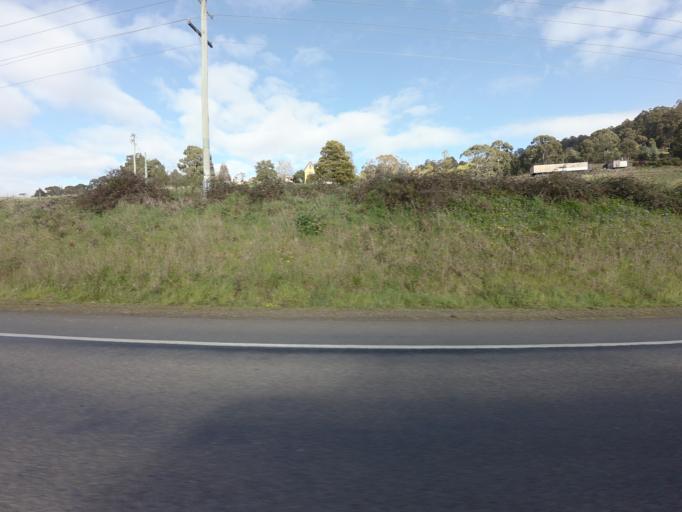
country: AU
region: Tasmania
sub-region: Huon Valley
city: Franklin
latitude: -43.1067
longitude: 147.0005
